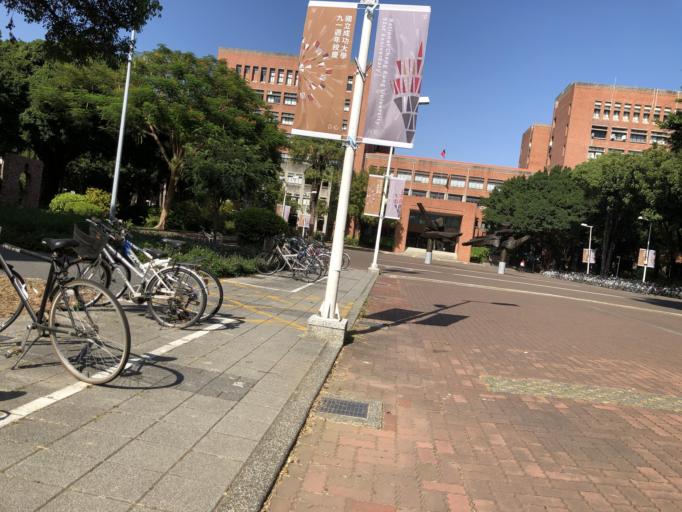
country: TW
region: Taiwan
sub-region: Tainan
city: Tainan
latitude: 22.9979
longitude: 120.2169
